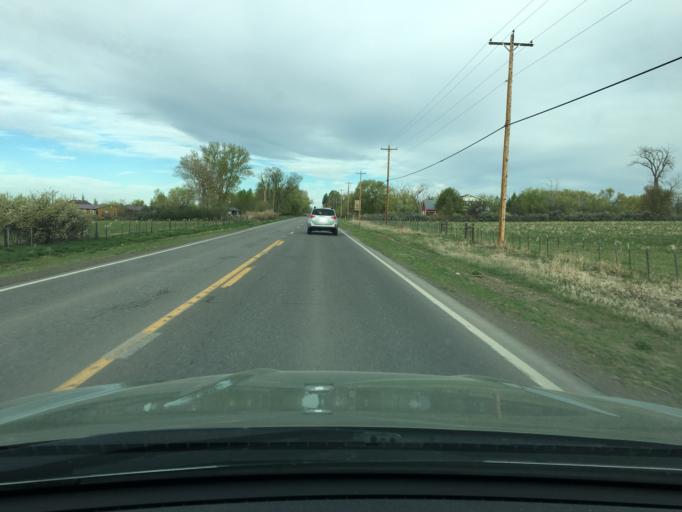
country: US
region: Colorado
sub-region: Delta County
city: Paonia
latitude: 38.8001
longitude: -107.7660
